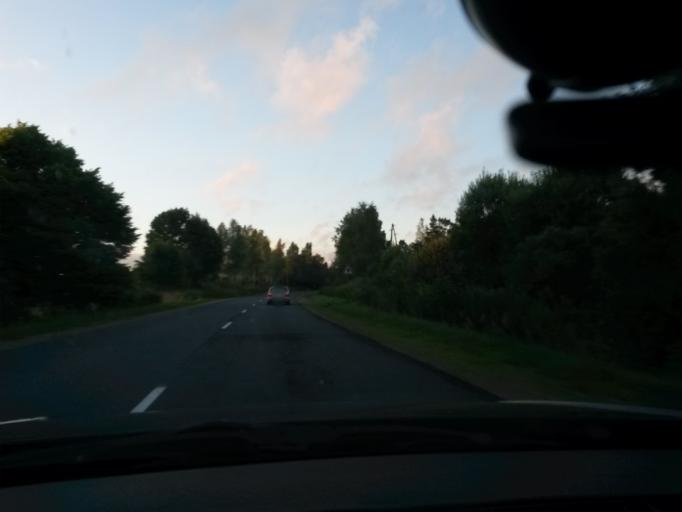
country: LV
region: Madonas Rajons
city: Madona
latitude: 56.7949
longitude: 26.0302
